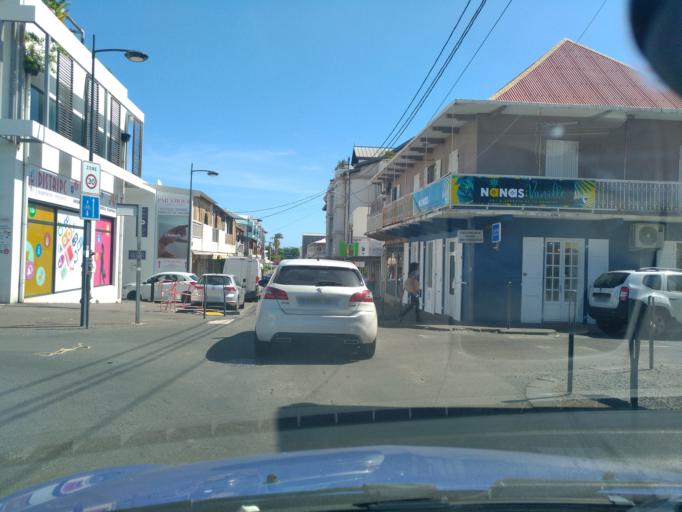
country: RE
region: Reunion
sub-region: Reunion
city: Saint-Pierre
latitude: -21.3411
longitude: 55.4739
